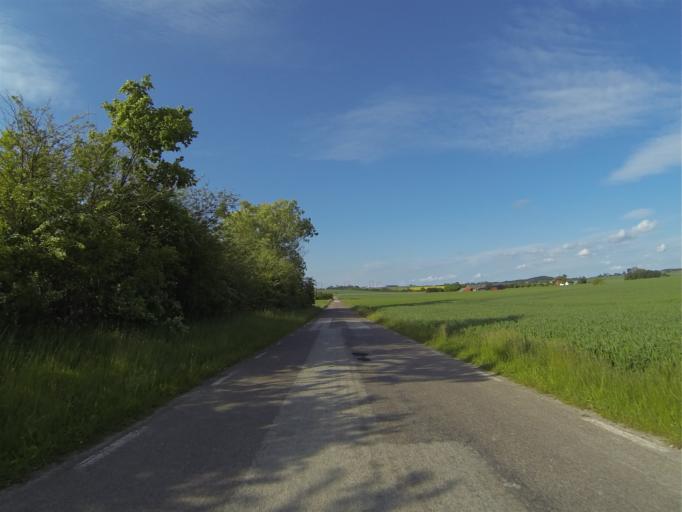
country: SE
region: Skane
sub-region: Staffanstorps Kommun
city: Staffanstorp
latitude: 55.6743
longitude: 13.2796
